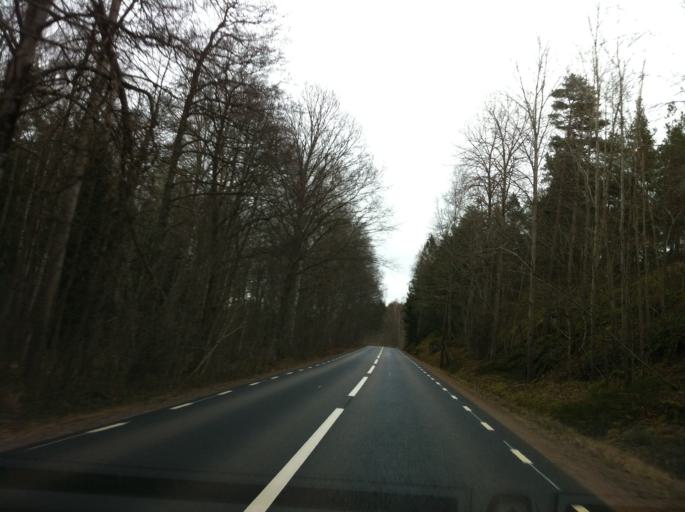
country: SE
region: Kalmar
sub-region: Vasterviks Kommun
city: Overum
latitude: 57.9086
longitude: 16.2033
